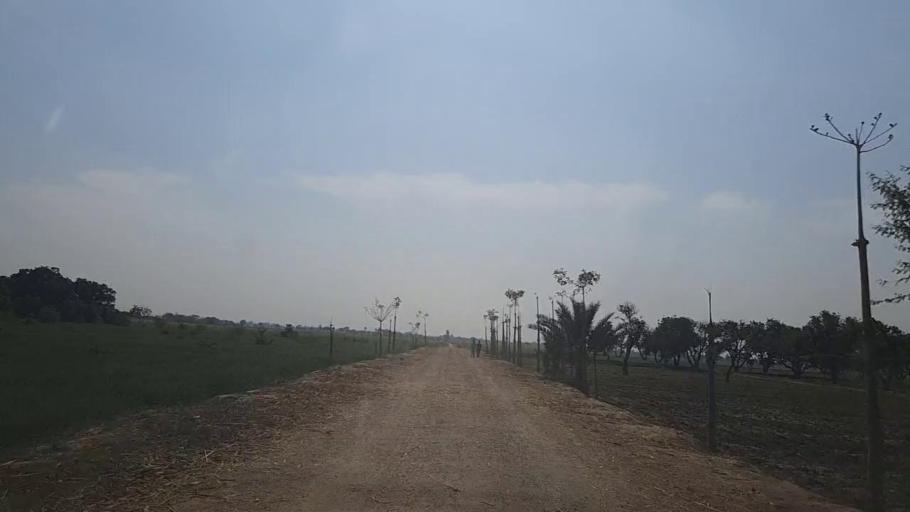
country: PK
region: Sindh
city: Mirpur Khas
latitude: 25.4925
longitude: 68.9440
